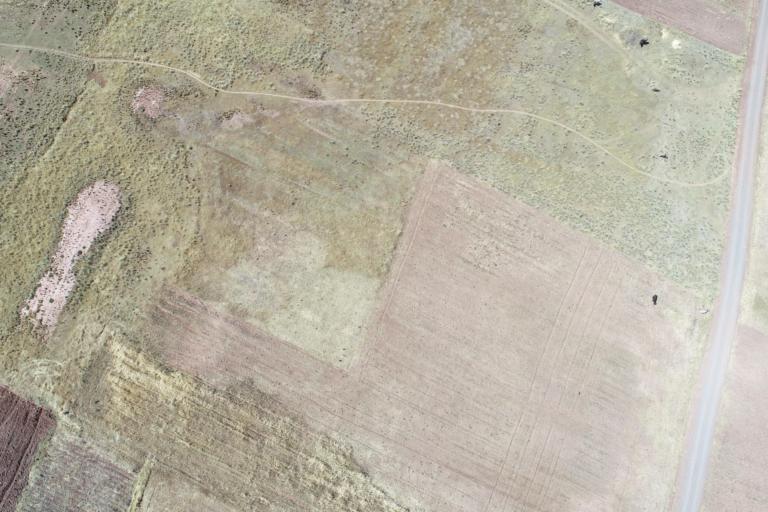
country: BO
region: La Paz
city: Tiahuanaco
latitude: -16.5937
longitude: -68.7708
